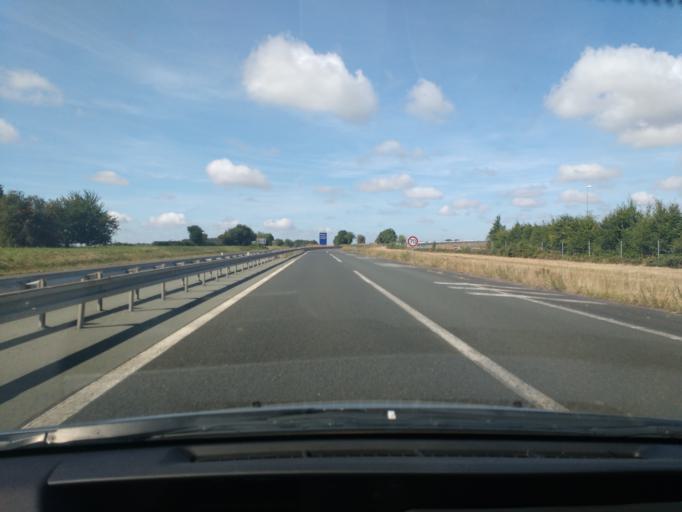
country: FR
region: Pays de la Loire
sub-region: Departement de Maine-et-Loire
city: Saint-Lambert-la-Potherie
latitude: 47.4656
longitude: -0.6860
